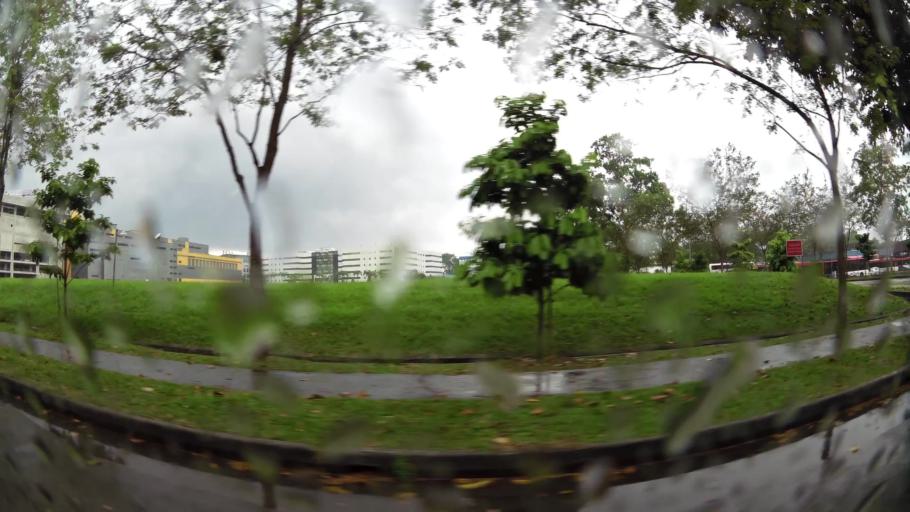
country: MY
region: Johor
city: Kampung Pasir Gudang Baru
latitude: 1.3875
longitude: 103.8463
